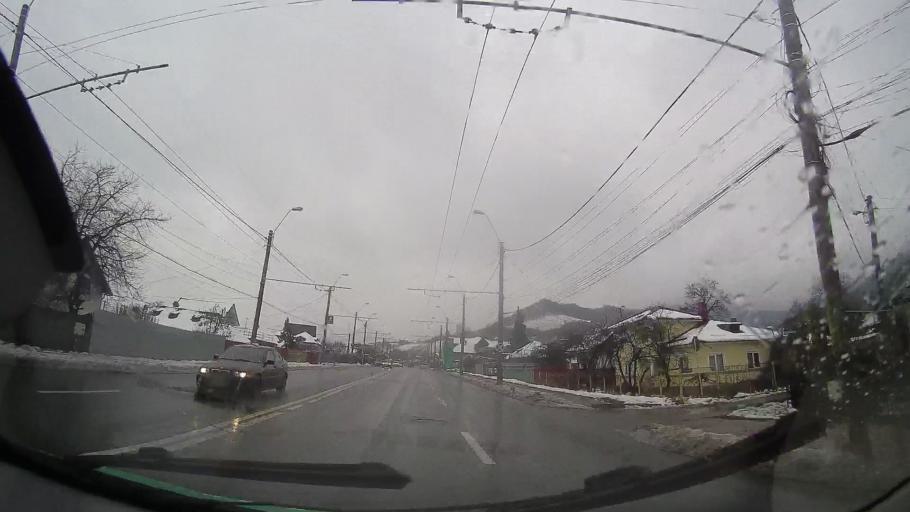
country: RO
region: Neamt
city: Piatra Neamt
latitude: 46.9398
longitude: 26.3328
